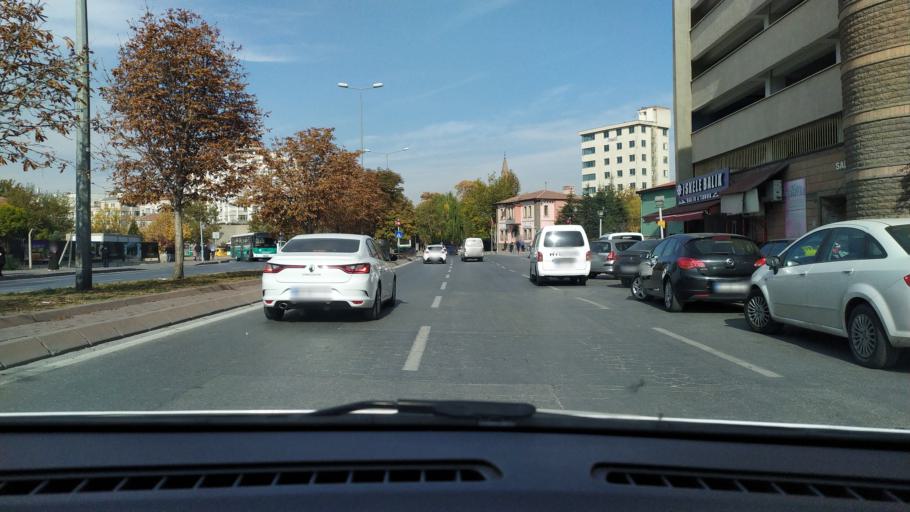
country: TR
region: Kayseri
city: Kayseri
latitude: 38.7158
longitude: 35.4913
